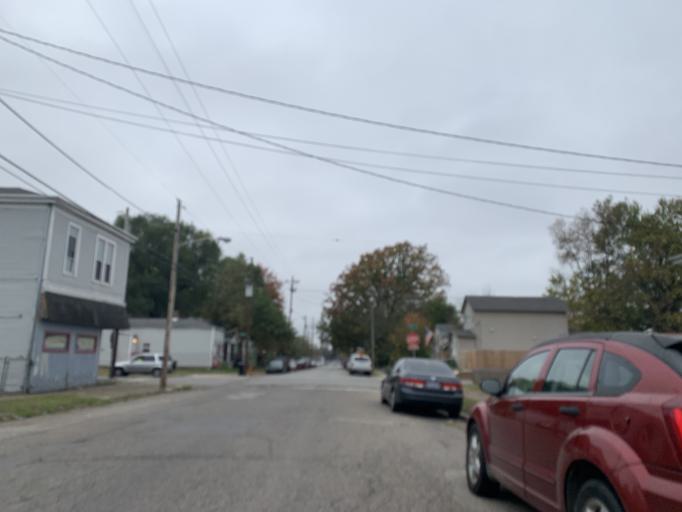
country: US
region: Kentucky
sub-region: Jefferson County
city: Louisville
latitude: 38.2616
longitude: -85.7890
